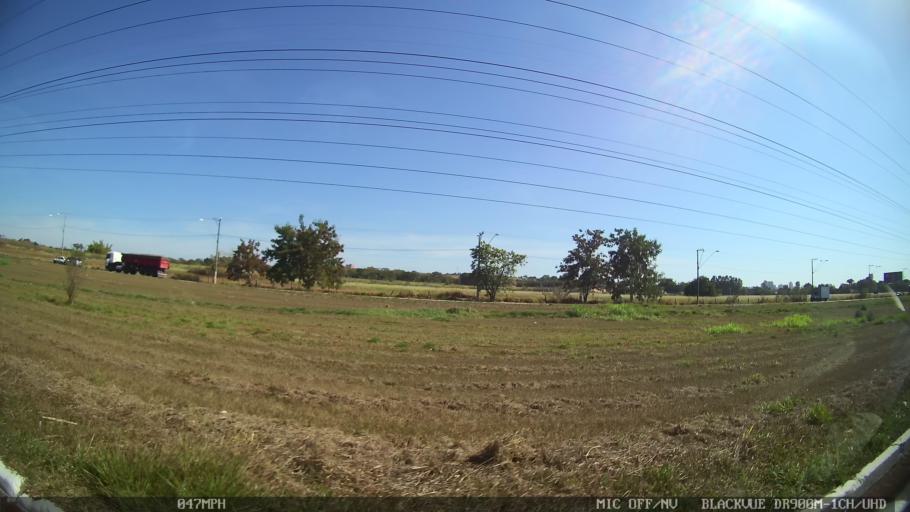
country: BR
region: Sao Paulo
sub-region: Ribeirao Preto
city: Ribeirao Preto
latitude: -21.2199
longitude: -47.7705
